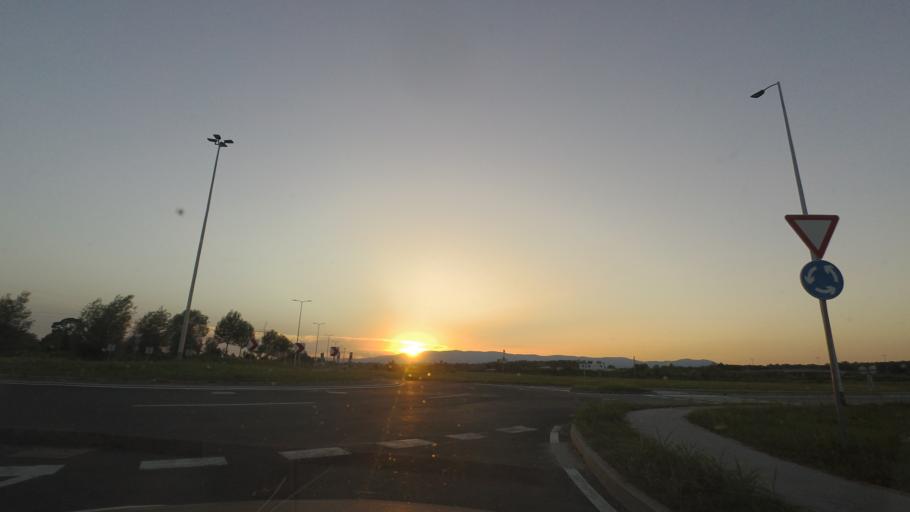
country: HR
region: Grad Zagreb
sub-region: Sesvete
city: Sesvete
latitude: 45.7930
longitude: 16.1471
